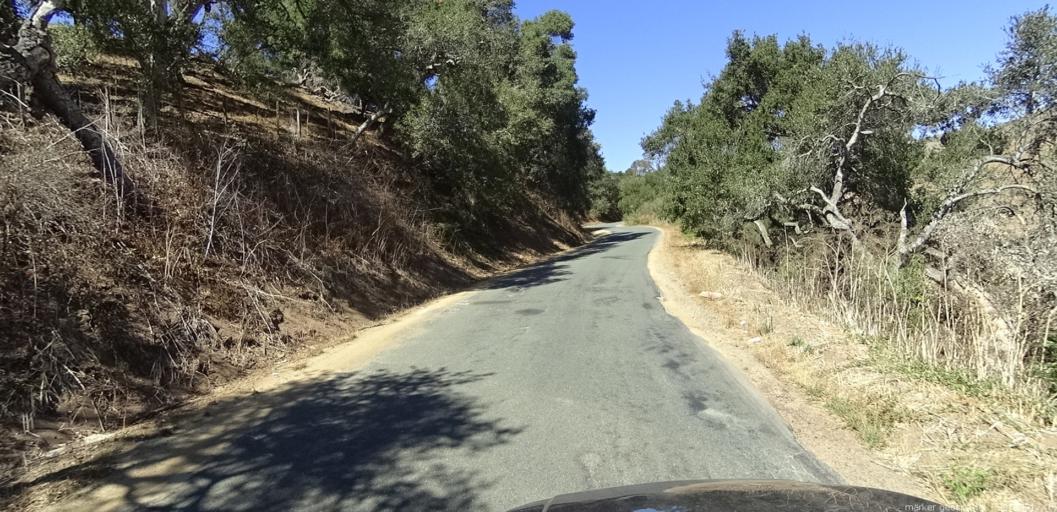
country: US
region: California
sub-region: San Benito County
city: San Juan Bautista
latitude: 36.8035
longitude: -121.5810
